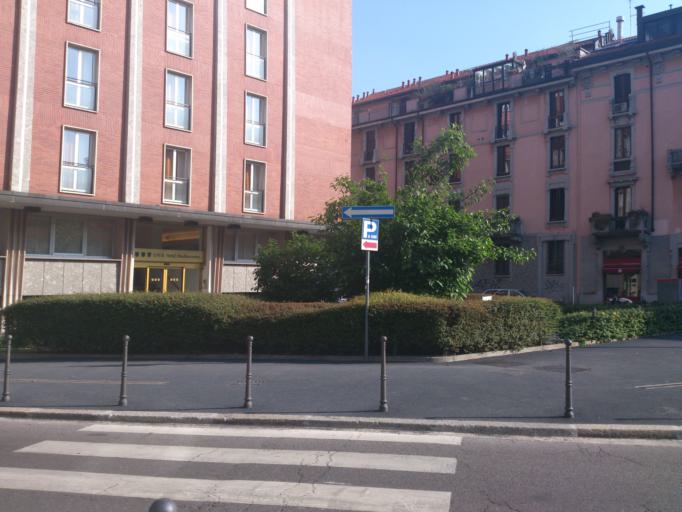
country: IT
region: Lombardy
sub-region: Citta metropolitana di Milano
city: Milano
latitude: 45.4521
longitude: 9.2057
